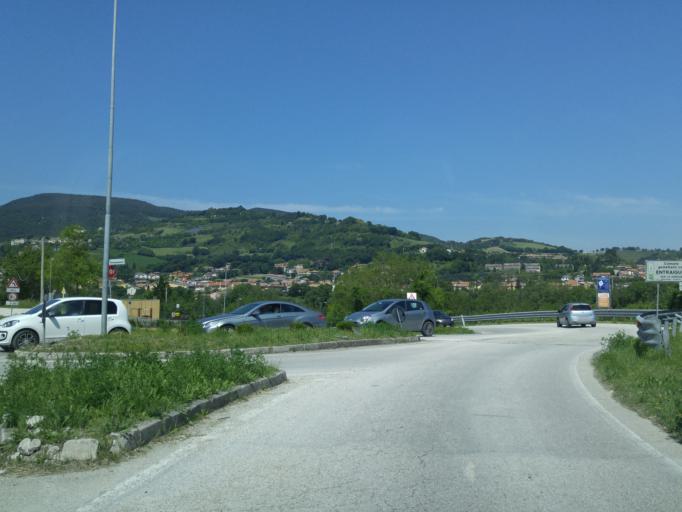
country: IT
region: The Marches
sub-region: Provincia di Pesaro e Urbino
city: Fossombrone
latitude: 43.6890
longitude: 12.8277
